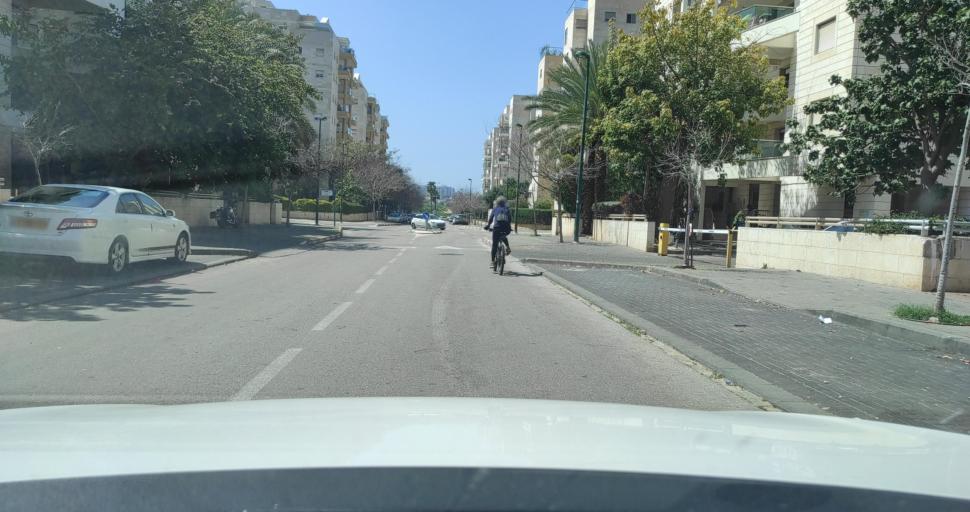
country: IL
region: Central District
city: Nordiyya
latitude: 32.2977
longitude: 34.8721
